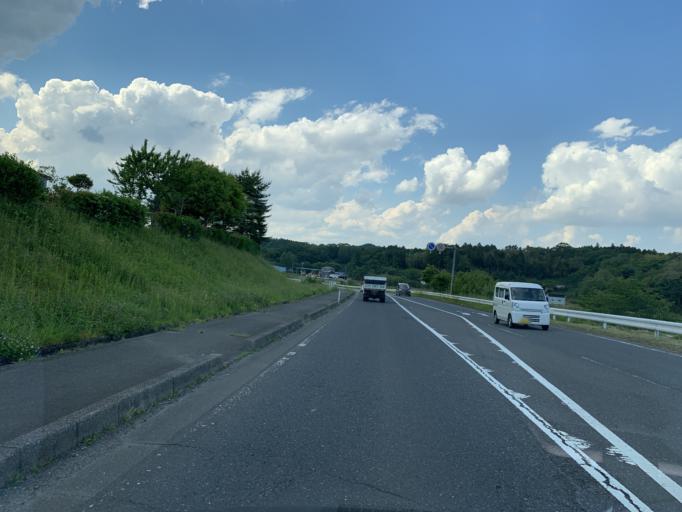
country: JP
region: Miyagi
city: Wakuya
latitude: 38.5405
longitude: 141.1498
